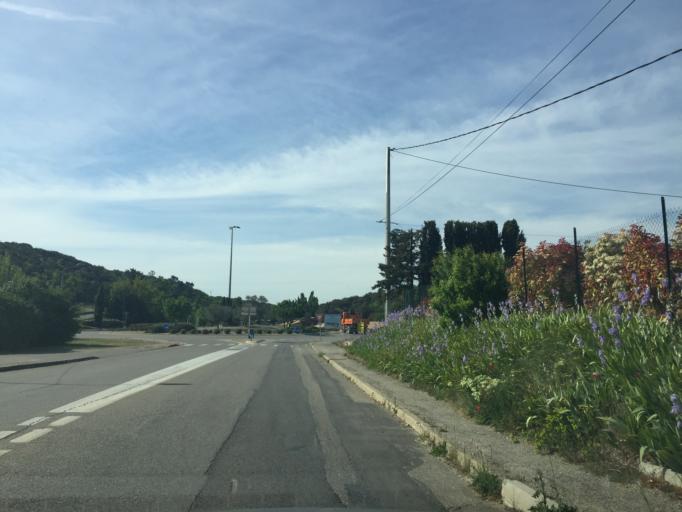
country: FR
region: Provence-Alpes-Cote d'Azur
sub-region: Departement du Var
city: Ginasservis
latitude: 43.6738
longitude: 5.8483
